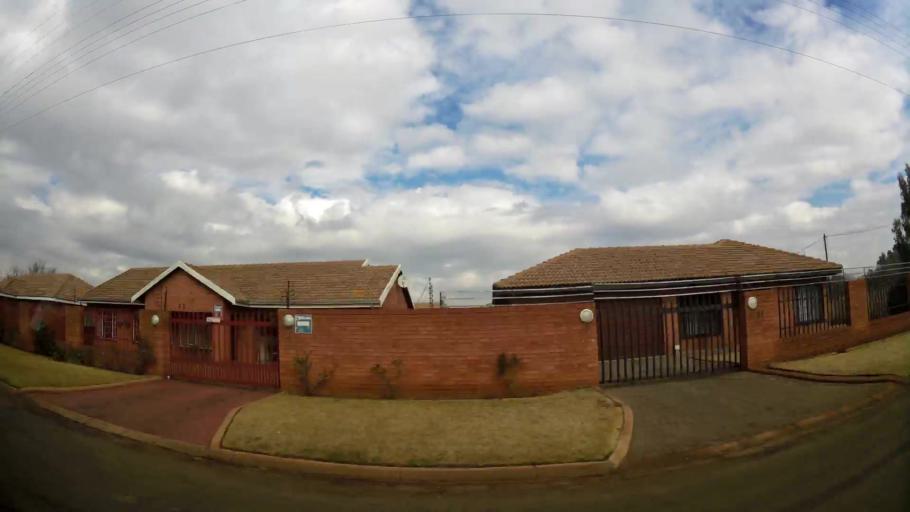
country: ZA
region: Gauteng
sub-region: Sedibeng District Municipality
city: Meyerton
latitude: -26.5860
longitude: 28.0133
